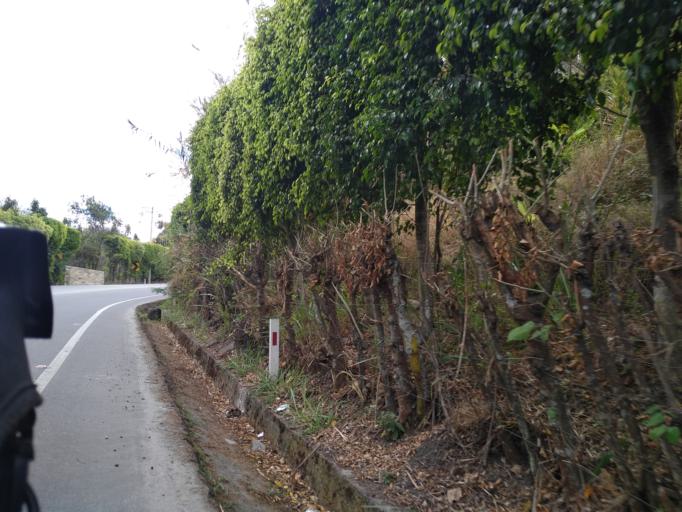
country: EC
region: Loja
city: Loja
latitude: -4.2123
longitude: -79.2315
